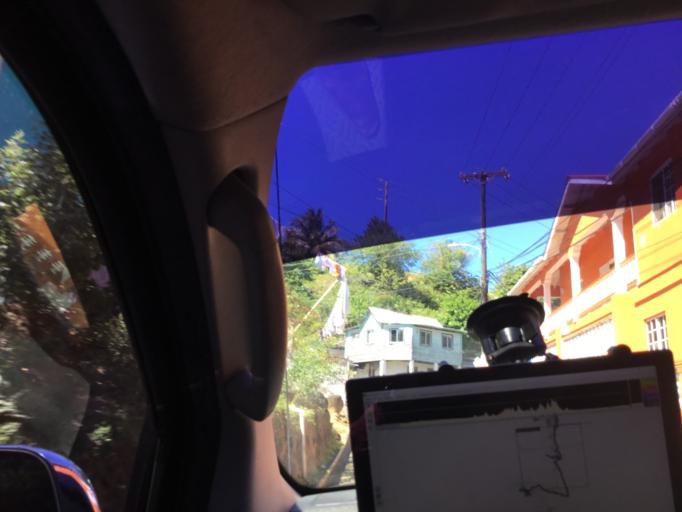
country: VC
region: Charlotte
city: Byera Village
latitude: 13.2457
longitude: -61.1413
